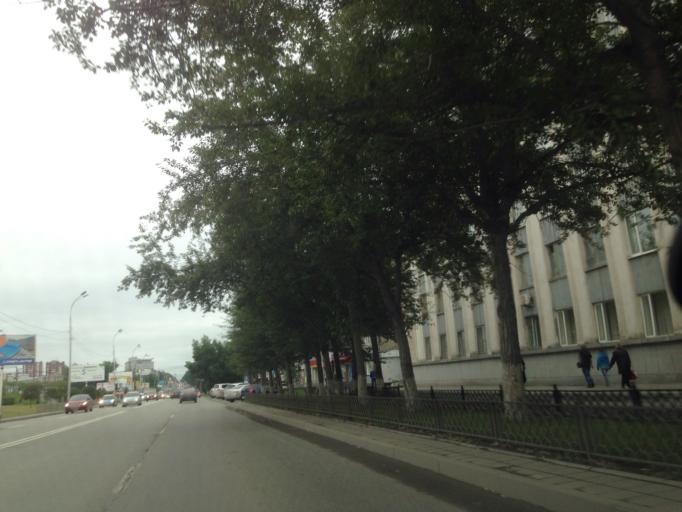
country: RU
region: Sverdlovsk
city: Yekaterinburg
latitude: 56.8406
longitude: 60.6324
